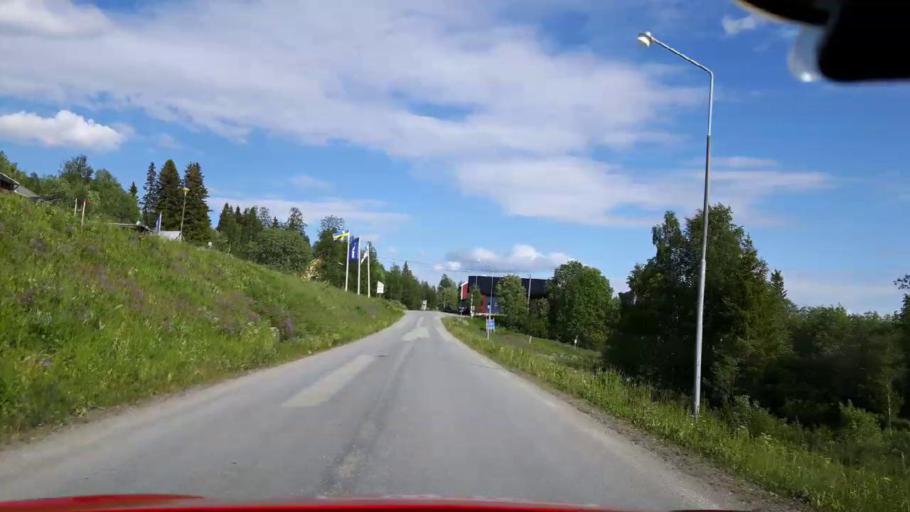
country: SE
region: Jaemtland
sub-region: Krokoms Kommun
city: Valla
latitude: 63.7659
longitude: 14.0741
